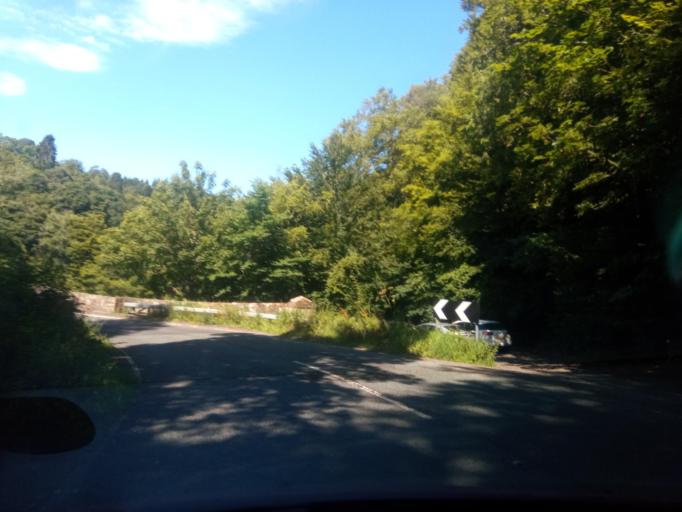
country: GB
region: England
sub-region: Northumberland
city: Bardon Mill
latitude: 54.9263
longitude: -2.3125
